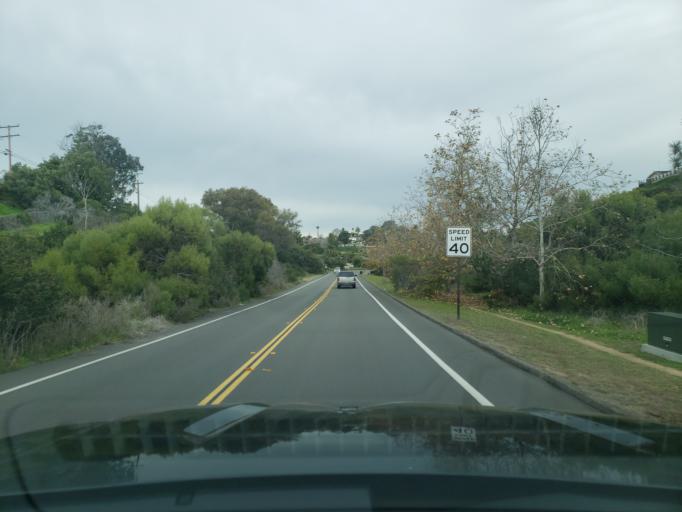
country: US
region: California
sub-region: San Diego County
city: Coronado
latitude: 32.7255
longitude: -117.2418
